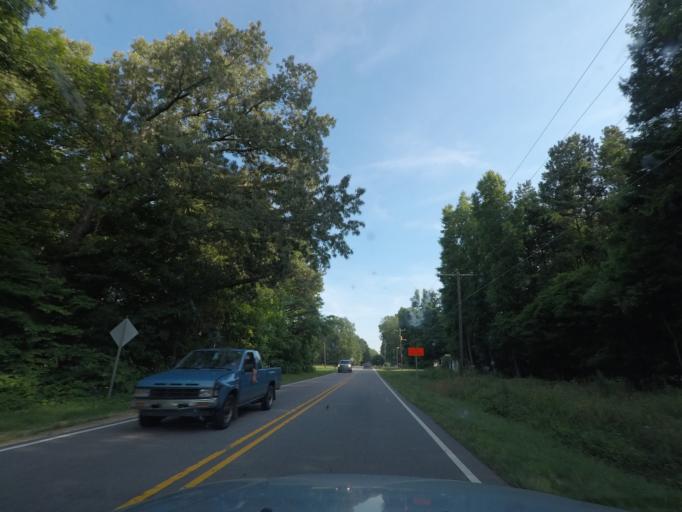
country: US
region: North Carolina
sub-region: Granville County
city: Oxford
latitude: 36.3928
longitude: -78.5928
